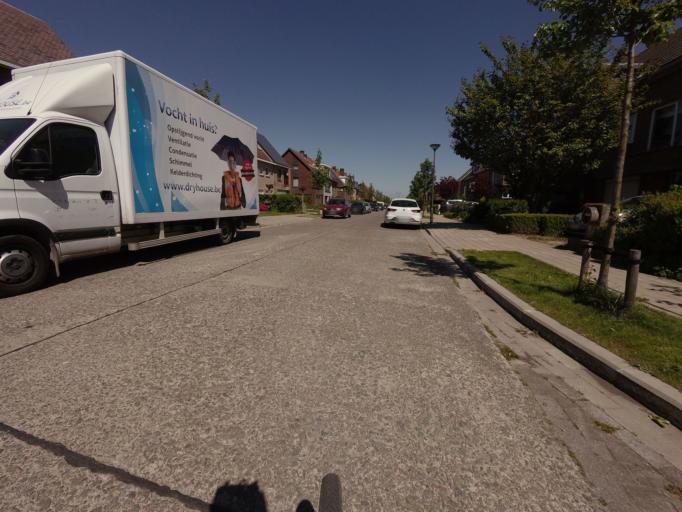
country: BE
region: Flanders
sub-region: Provincie Antwerpen
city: Hove
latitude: 51.1708
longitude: 4.4767
